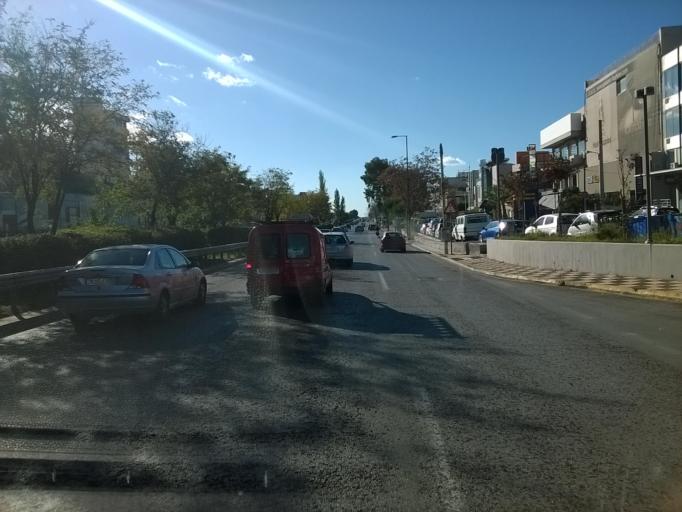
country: GR
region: Attica
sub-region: Nomarchia Athinas
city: Agios Dimitrios
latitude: 37.9291
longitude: 23.7442
